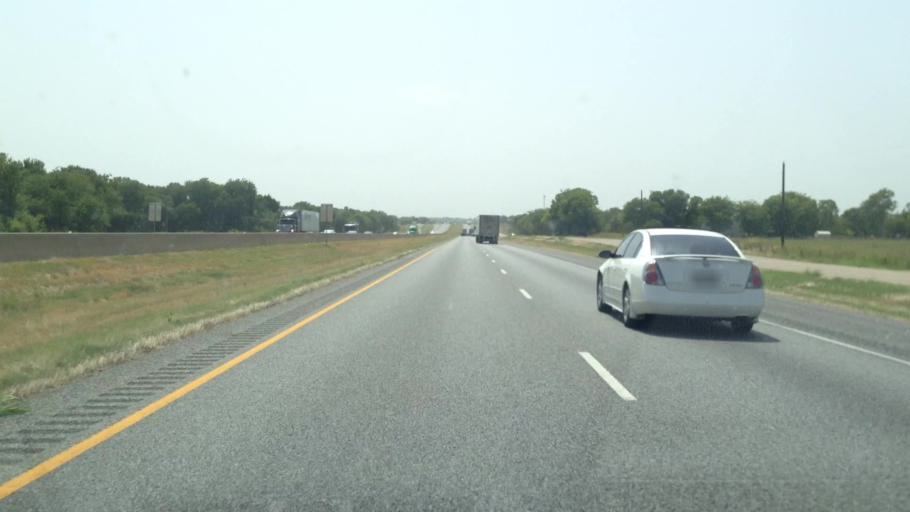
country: US
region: Texas
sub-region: Hunt County
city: Commerce
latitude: 33.1317
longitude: -95.9250
